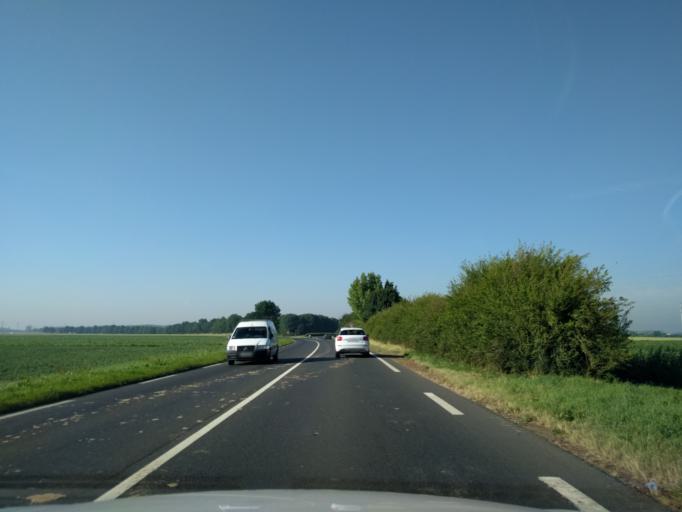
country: FR
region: Picardie
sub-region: Departement de la Somme
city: Roye
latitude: 49.7277
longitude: 2.8039
